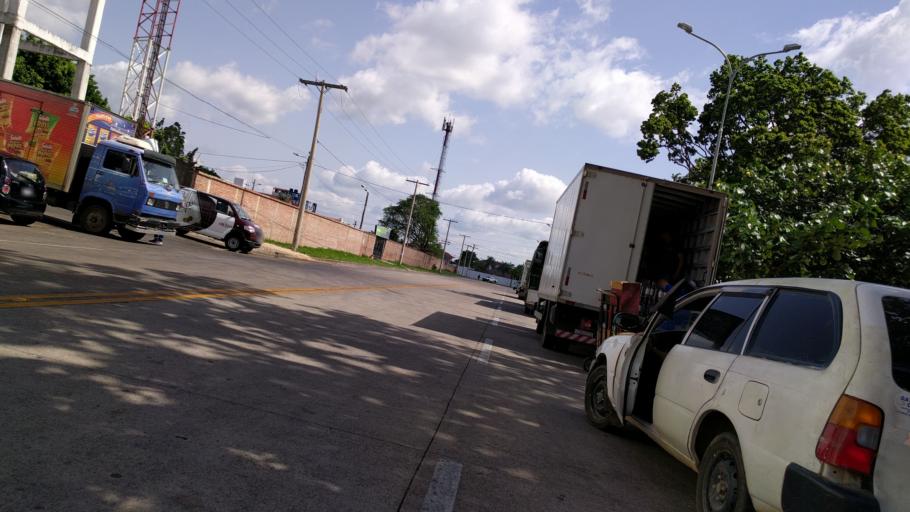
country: BO
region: Santa Cruz
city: Santa Cruz de la Sierra
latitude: -17.7848
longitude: -63.2115
